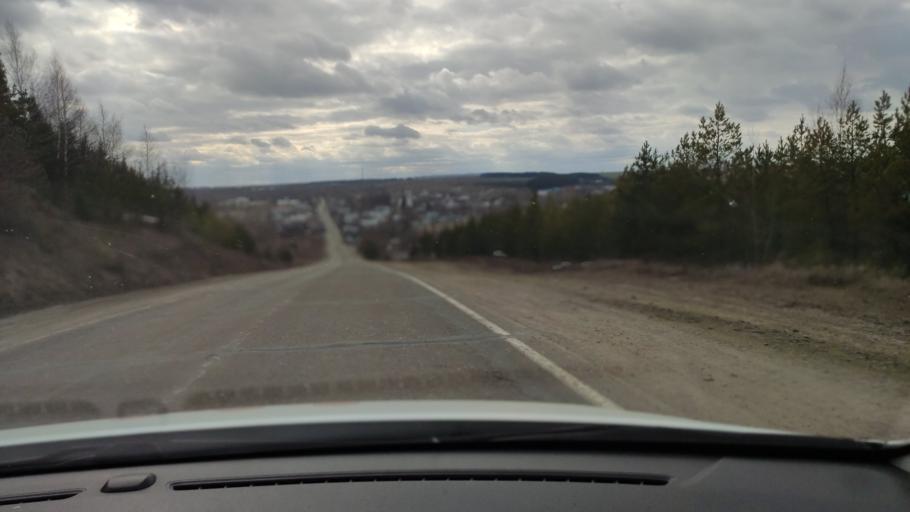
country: RU
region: Tatarstan
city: Vysokaya Gora
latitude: 56.1262
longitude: 49.2015
